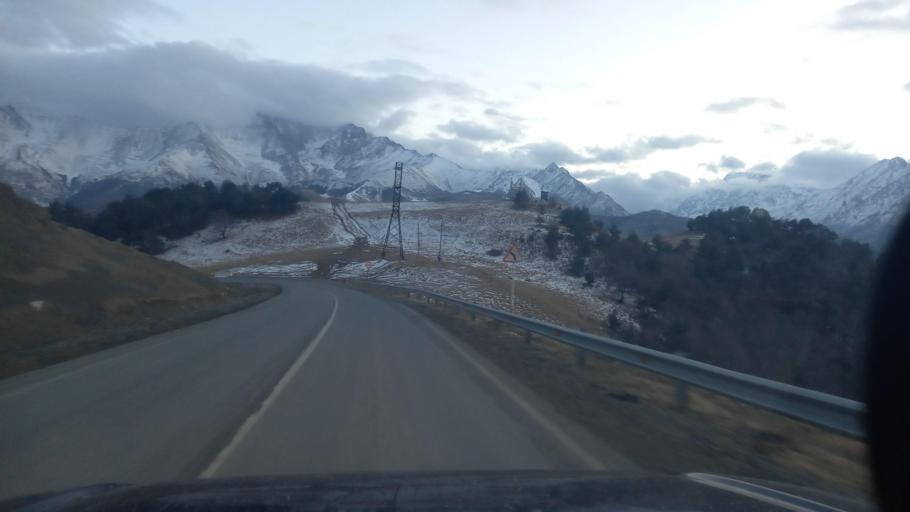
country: RU
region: Ingushetiya
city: Dzhayrakh
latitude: 42.8190
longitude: 44.8390
